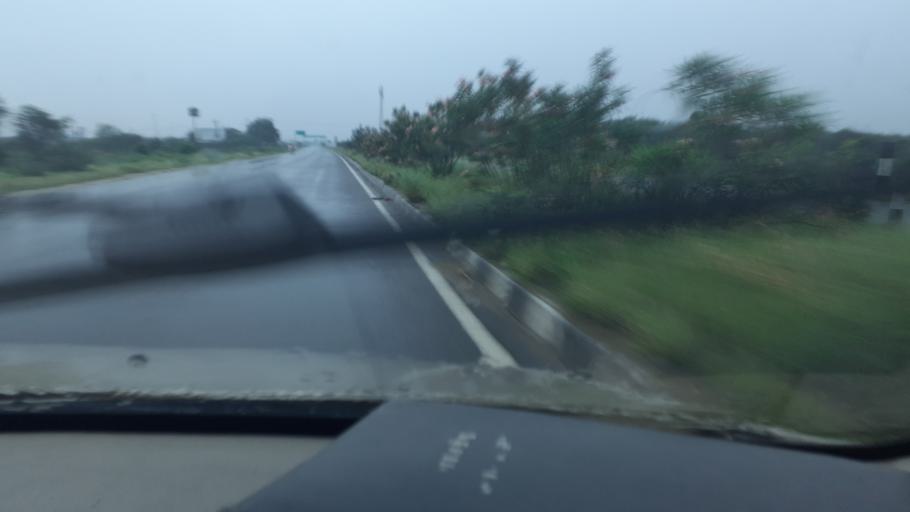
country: IN
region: Tamil Nadu
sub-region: Virudhunagar
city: Sattur
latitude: 9.3975
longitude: 77.9161
